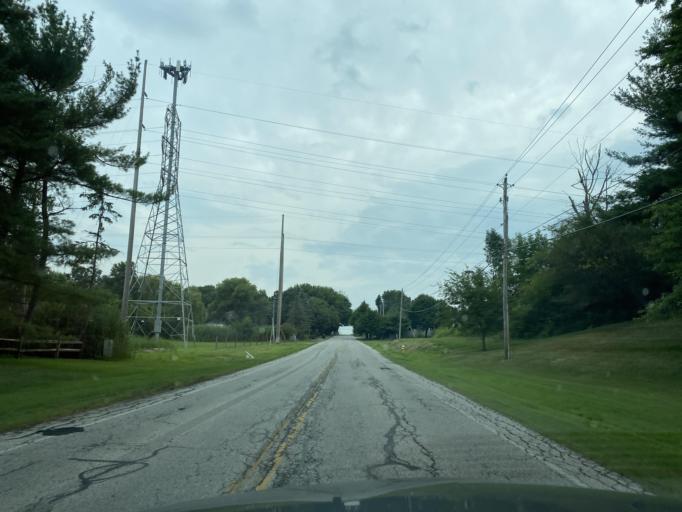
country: US
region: Ohio
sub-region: Summit County
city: Fairlawn
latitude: 41.1423
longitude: -81.5874
